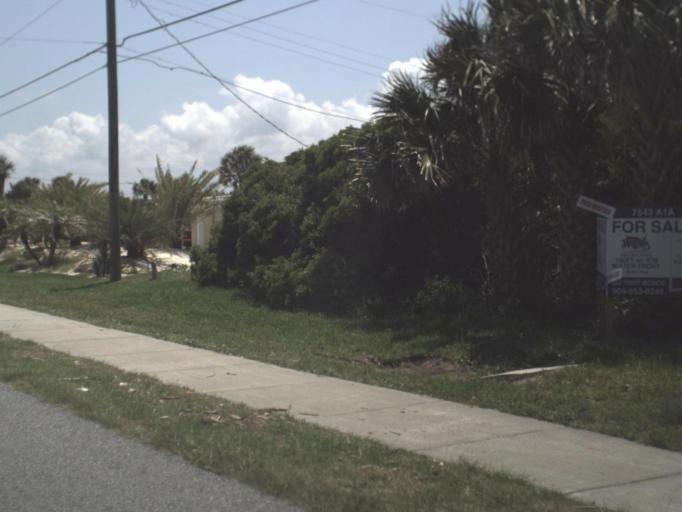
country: US
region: Florida
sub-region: Saint Johns County
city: Butler Beach
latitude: 29.7523
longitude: -81.2472
